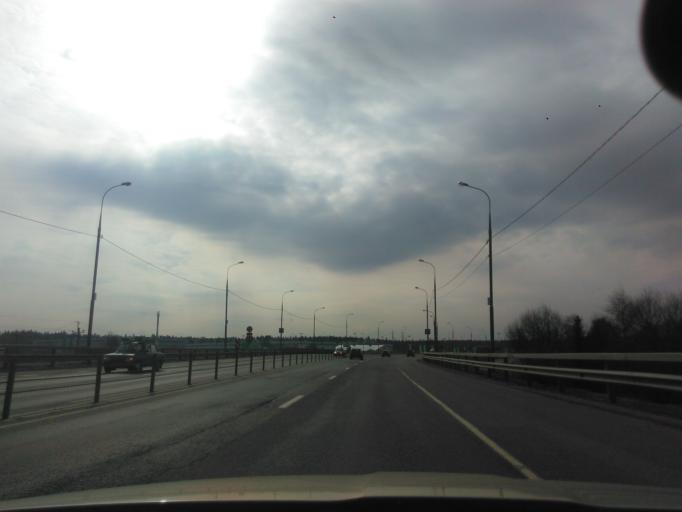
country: RU
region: Moskovskaya
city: Marfino
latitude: 56.0494
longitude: 37.5382
